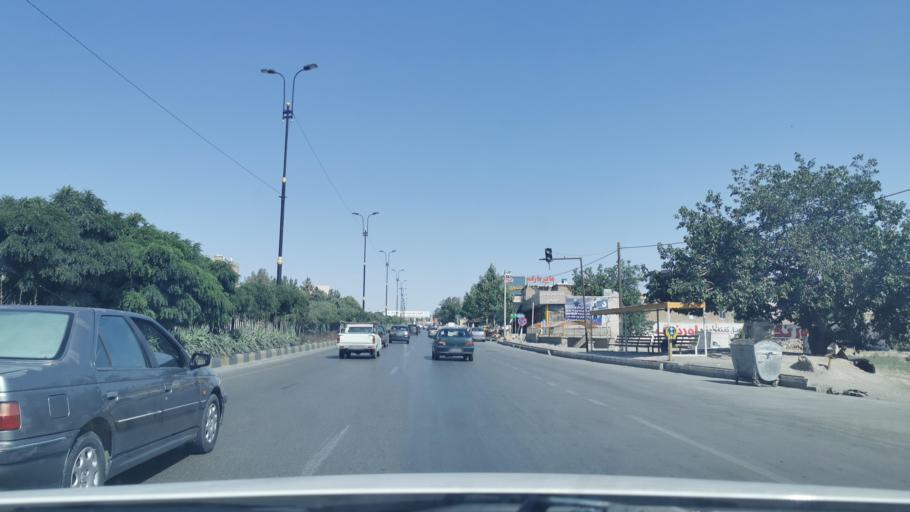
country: IR
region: Razavi Khorasan
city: Torqabeh
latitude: 36.3992
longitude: 59.3918
